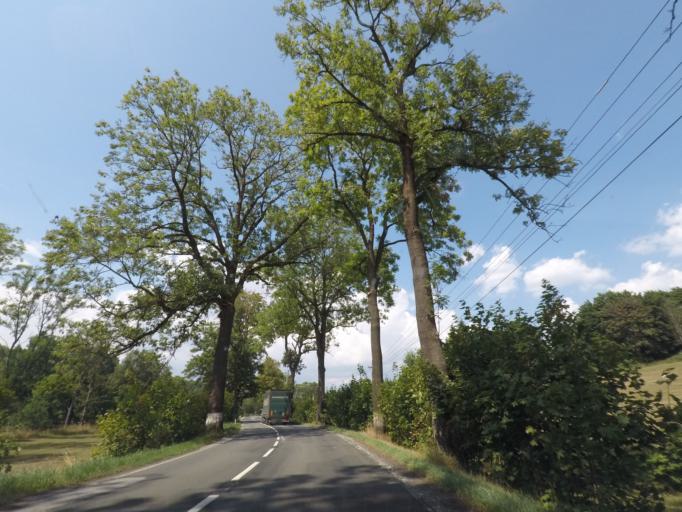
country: CZ
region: Kralovehradecky
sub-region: Okres Trutnov
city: Hostinne
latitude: 50.5189
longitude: 15.7282
